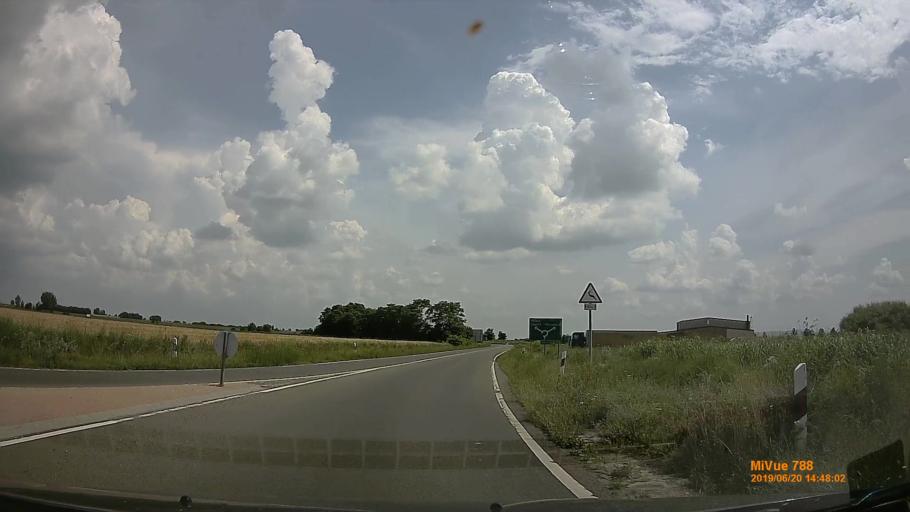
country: HU
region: Baranya
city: Kozarmisleny
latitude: 46.0177
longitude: 18.2881
